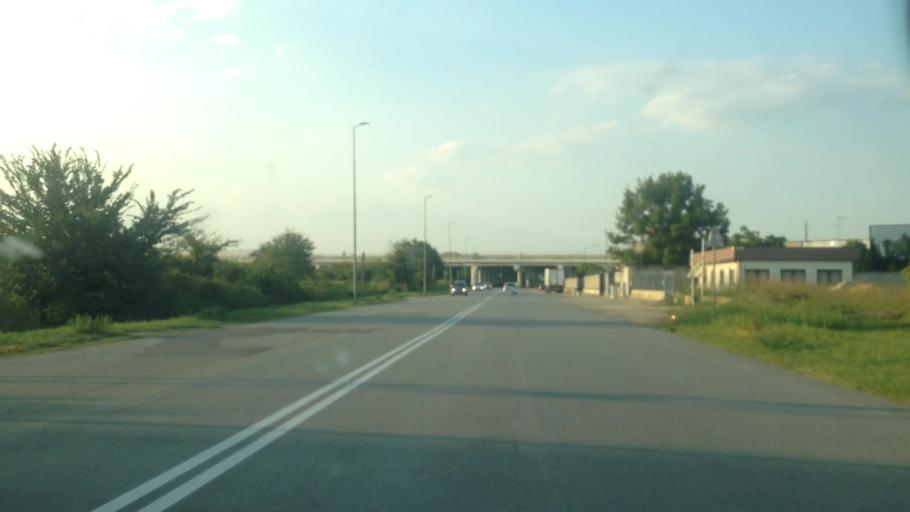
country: IT
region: Piedmont
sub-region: Provincia di Asti
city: Asti
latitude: 44.9107
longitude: 8.2301
